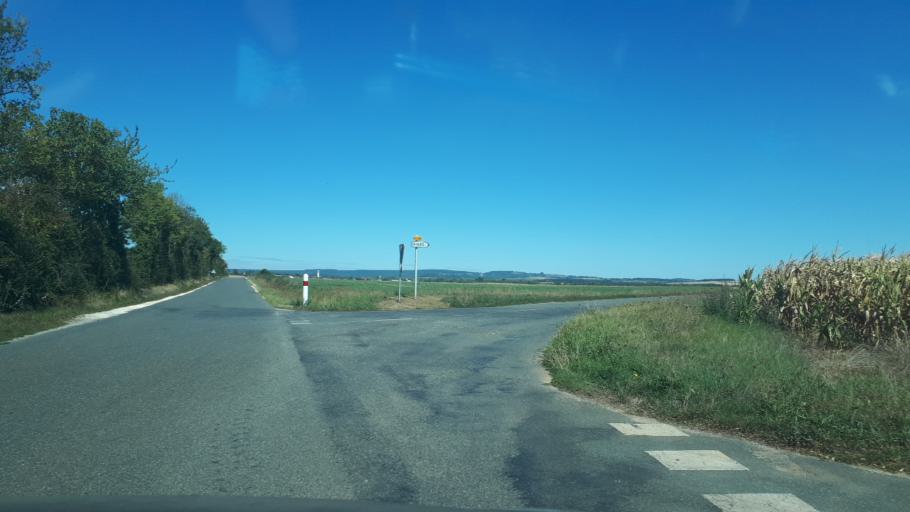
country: FR
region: Centre
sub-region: Departement du Cher
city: Sainte-Solange
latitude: 47.1736
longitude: 2.5690
